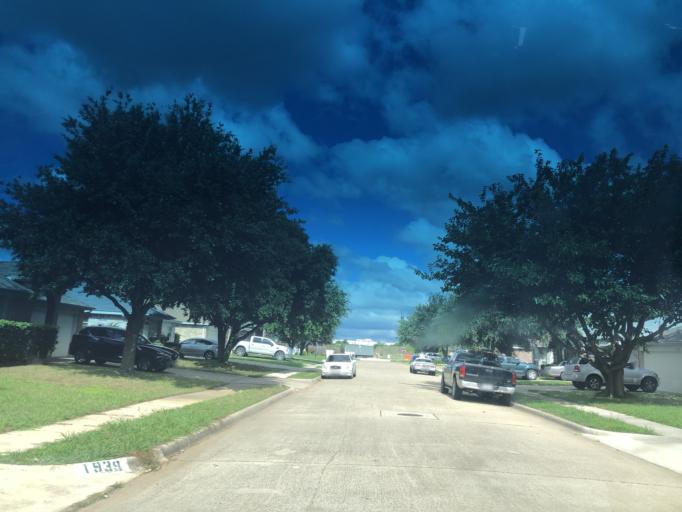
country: US
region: Texas
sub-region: Dallas County
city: Grand Prairie
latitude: 32.6998
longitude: -97.0314
